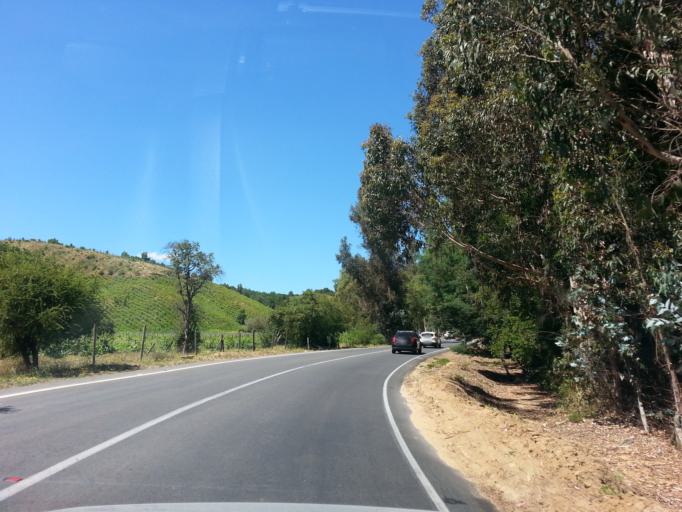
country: CL
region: Valparaiso
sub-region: Provincia de Marga Marga
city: Villa Alemana
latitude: -33.1868
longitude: -71.3686
